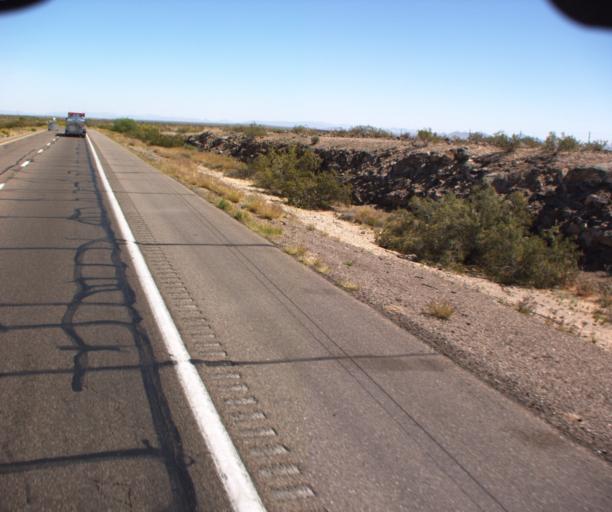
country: US
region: Arizona
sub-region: Maricopa County
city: Gila Bend
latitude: 32.8906
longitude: -113.0598
